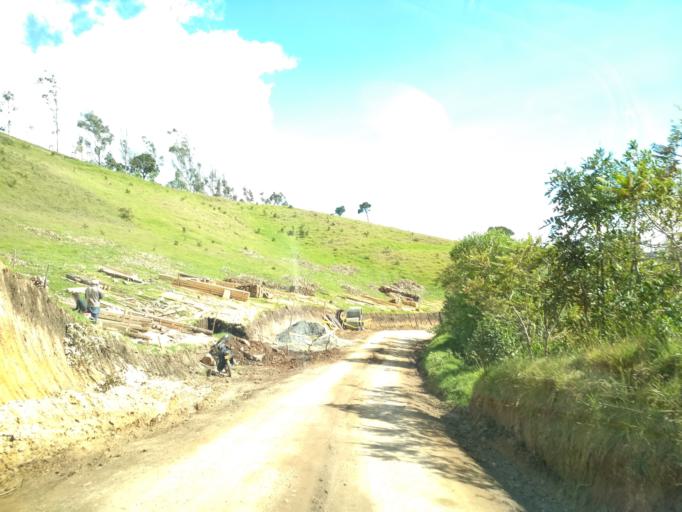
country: CO
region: Cauca
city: Jambalo
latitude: 2.7027
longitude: -76.3291
